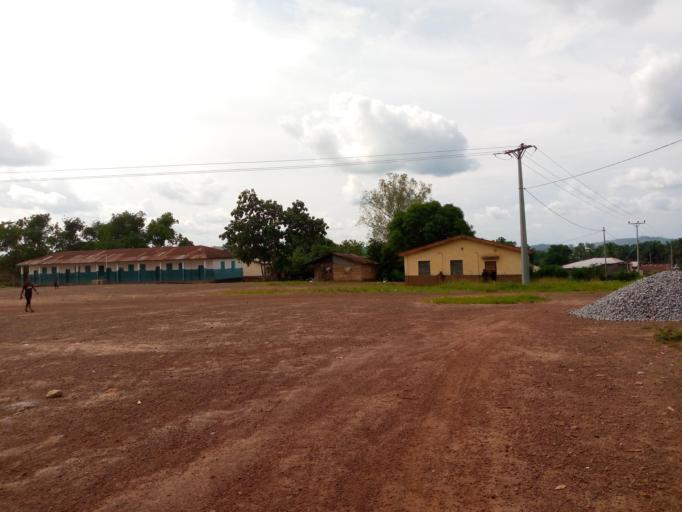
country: SL
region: Northern Province
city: Magburaka
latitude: 8.7217
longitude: -11.9401
